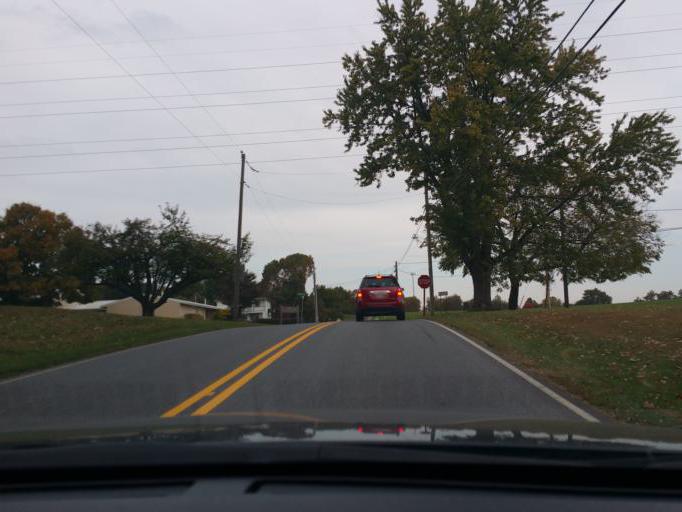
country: US
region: Pennsylvania
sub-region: Lancaster County
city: Willow Street
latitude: 40.0152
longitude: -76.2763
